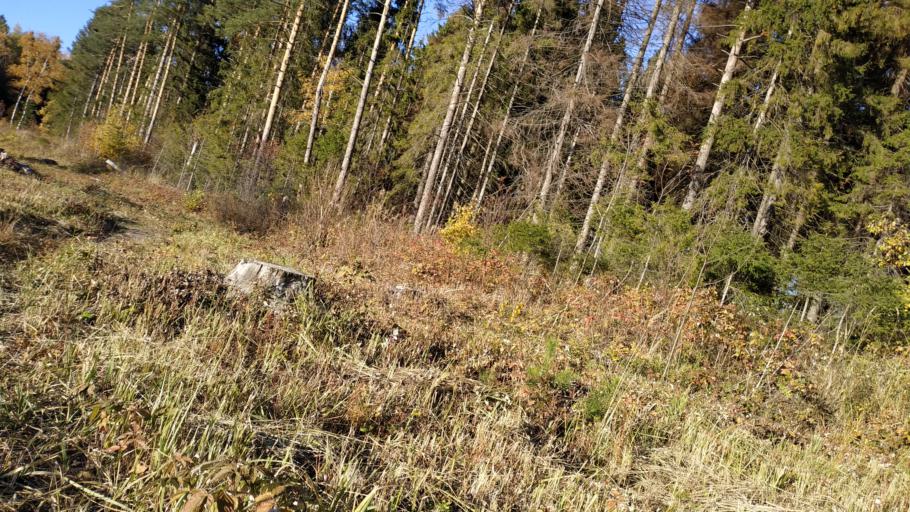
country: RU
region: Moskovskaya
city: Lobnya
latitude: 55.9994
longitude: 37.4616
